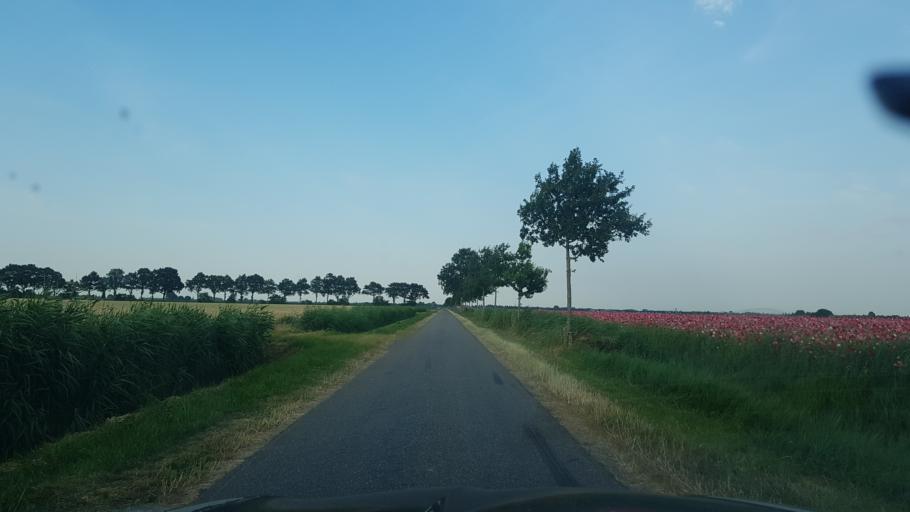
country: NL
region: Zeeland
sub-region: Gemeente Tholen
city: Tholen
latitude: 51.5326
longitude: 4.1470
